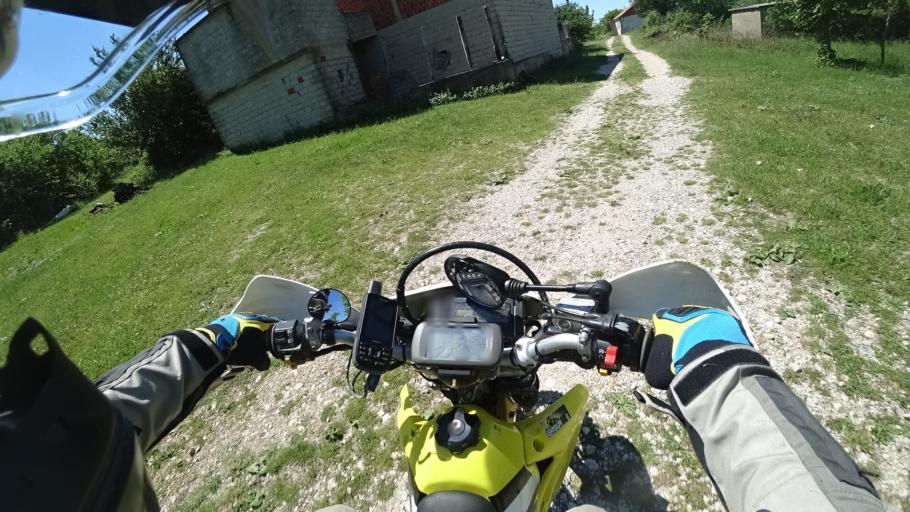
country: HR
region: Sibensko-Kniniska
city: Knin
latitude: 44.0112
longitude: 16.3245
